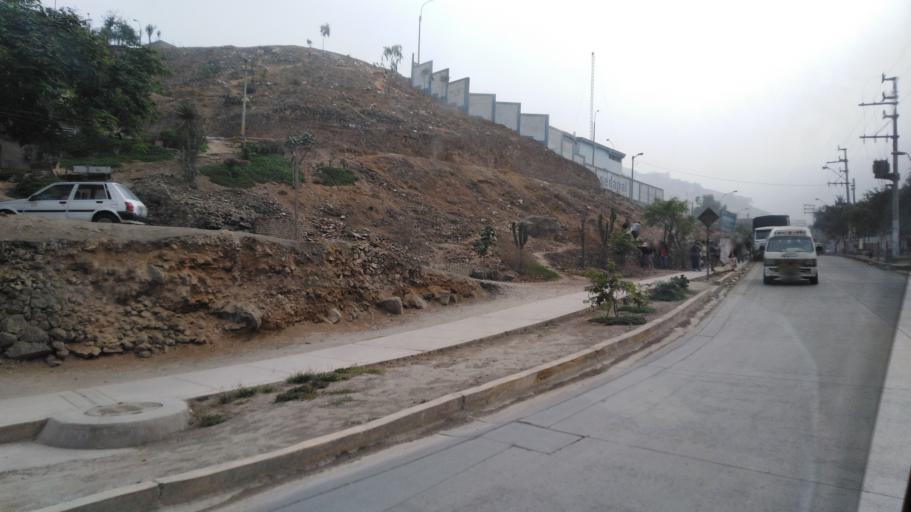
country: PE
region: Lima
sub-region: Lima
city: La Molina
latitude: -12.1481
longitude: -76.9334
